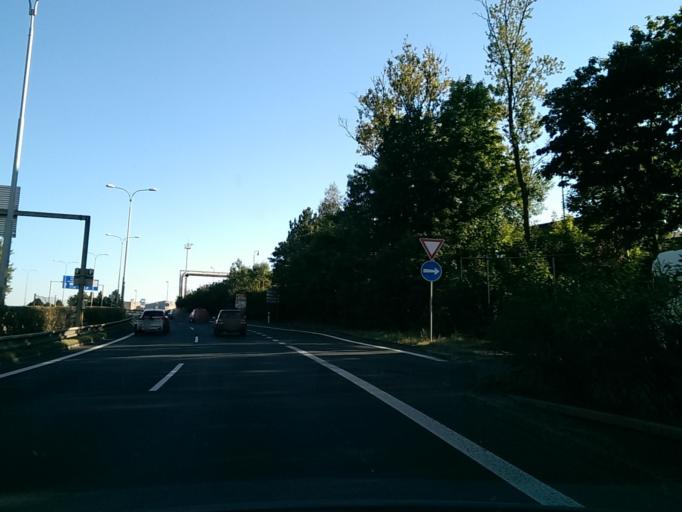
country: CZ
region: Liberecky
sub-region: Okres Liberec
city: Liberec
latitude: 50.7609
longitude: 15.0484
